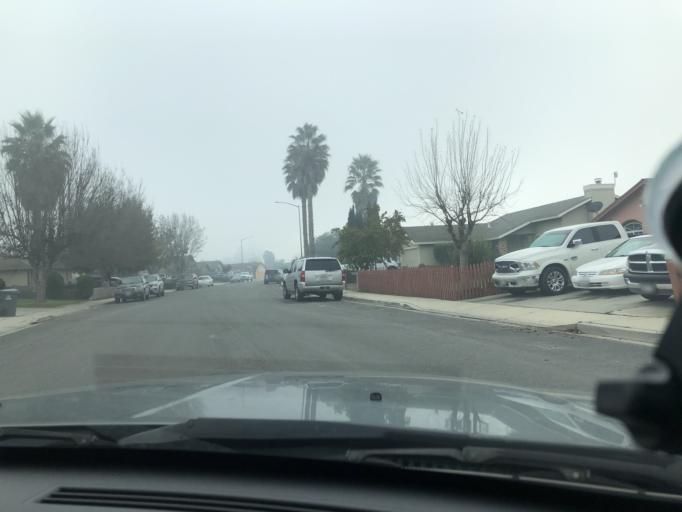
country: US
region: California
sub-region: Monterey County
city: King City
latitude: 36.2077
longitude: -121.1452
